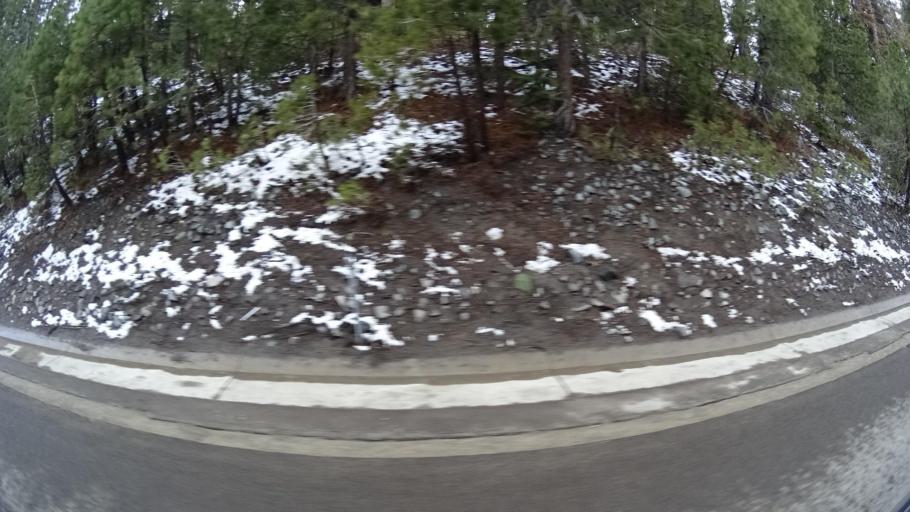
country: US
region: Nevada
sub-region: Washoe County
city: Incline Village
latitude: 39.2715
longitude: -119.9505
